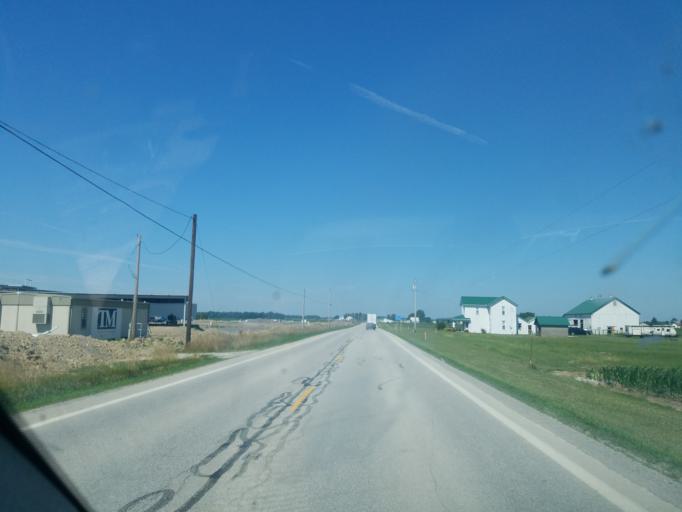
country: US
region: Ohio
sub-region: Shelby County
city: Jackson Center
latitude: 40.4397
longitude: -84.0603
